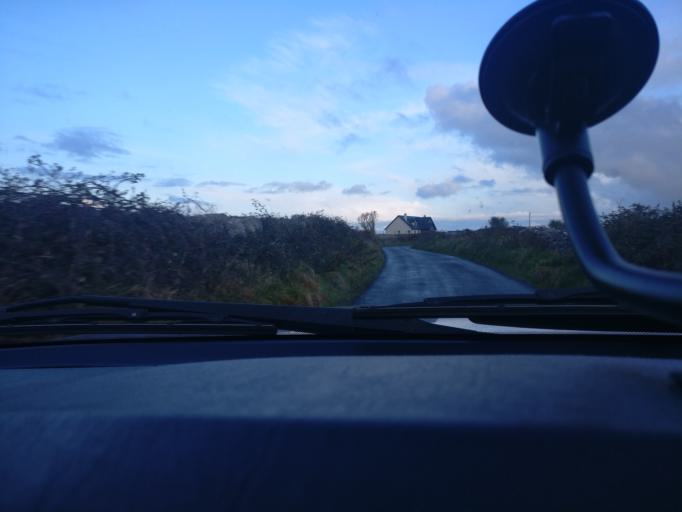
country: IE
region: Connaught
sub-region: County Galway
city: Athenry
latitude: 53.1980
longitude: -8.6867
